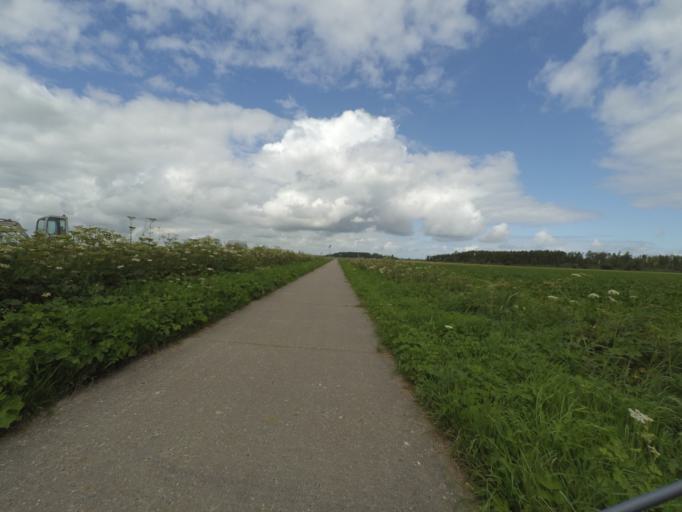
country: NL
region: Groningen
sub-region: Gemeente Zuidhorn
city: Grijpskerk
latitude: 53.3172
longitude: 6.2568
